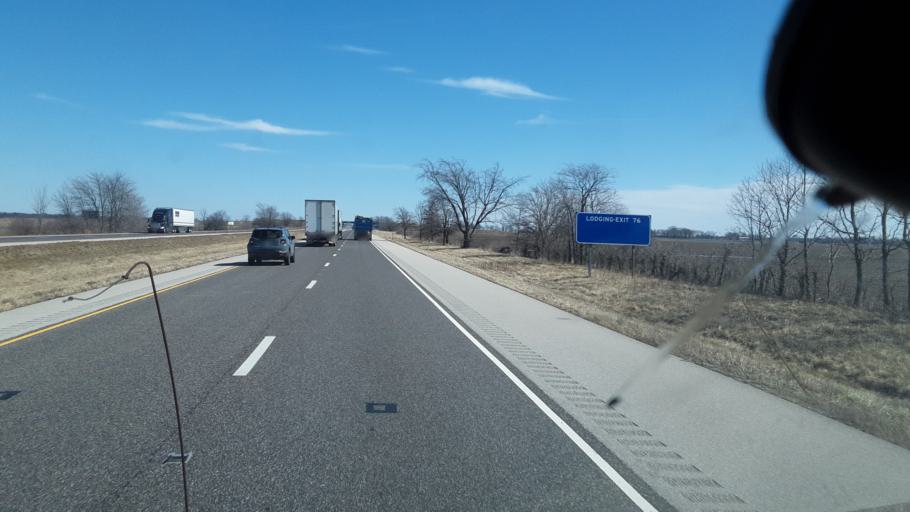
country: US
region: Illinois
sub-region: Fayette County
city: Saint Elmo
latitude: 39.0022
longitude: -88.8883
